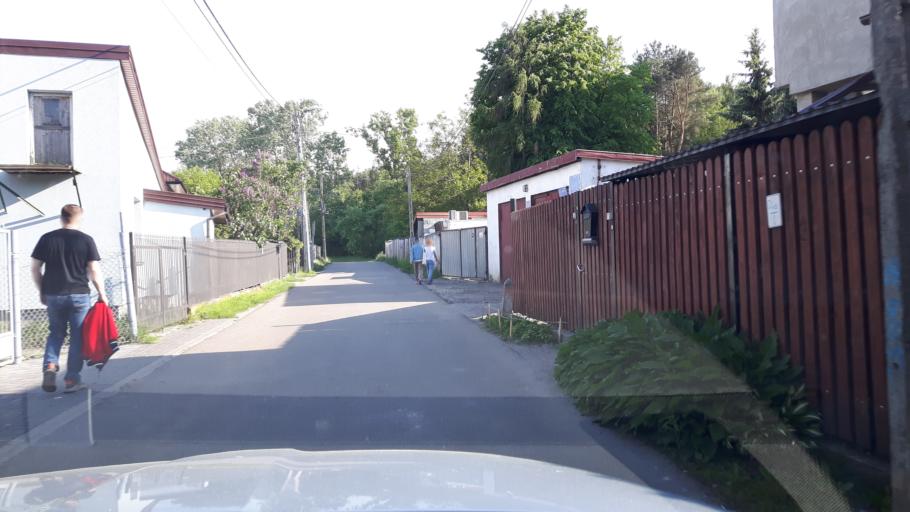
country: PL
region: Masovian Voivodeship
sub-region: Warszawa
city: Praga Poludnie
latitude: 52.2532
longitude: 21.1210
